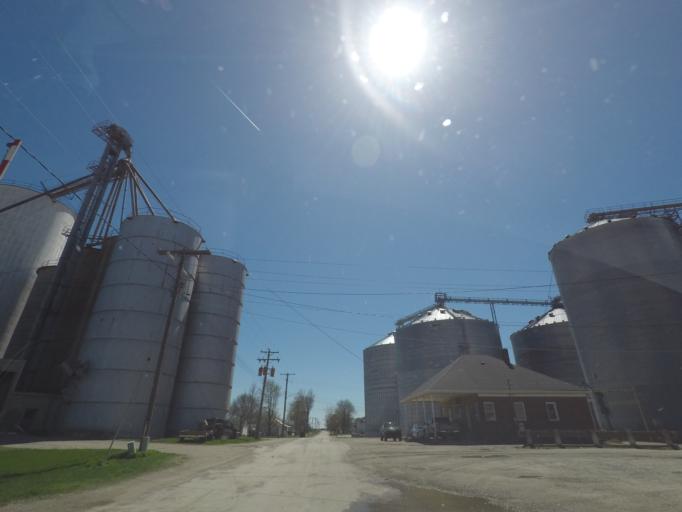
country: US
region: Illinois
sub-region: Macon County
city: Warrensburg
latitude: 39.9660
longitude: -89.1627
